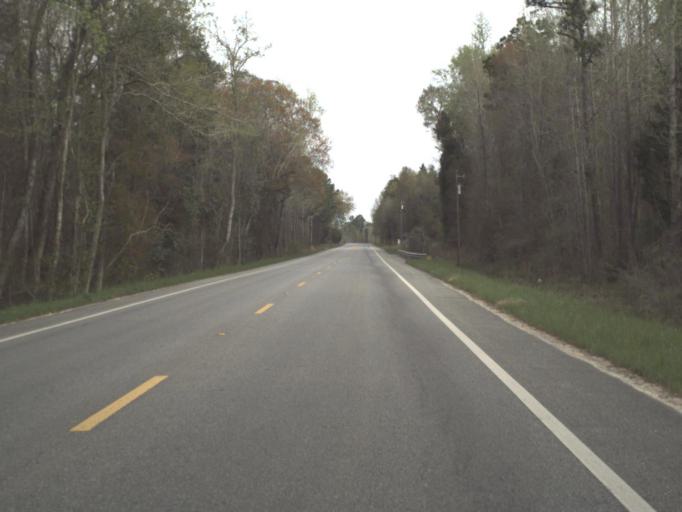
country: US
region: Florida
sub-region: Holmes County
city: Bonifay
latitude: 30.8547
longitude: -85.6666
